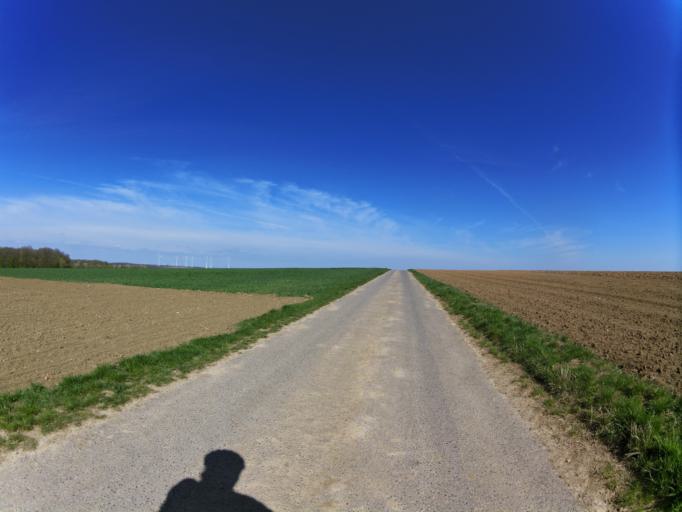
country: DE
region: Bavaria
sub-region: Regierungsbezirk Unterfranken
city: Winterhausen
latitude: 49.6896
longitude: 10.0022
